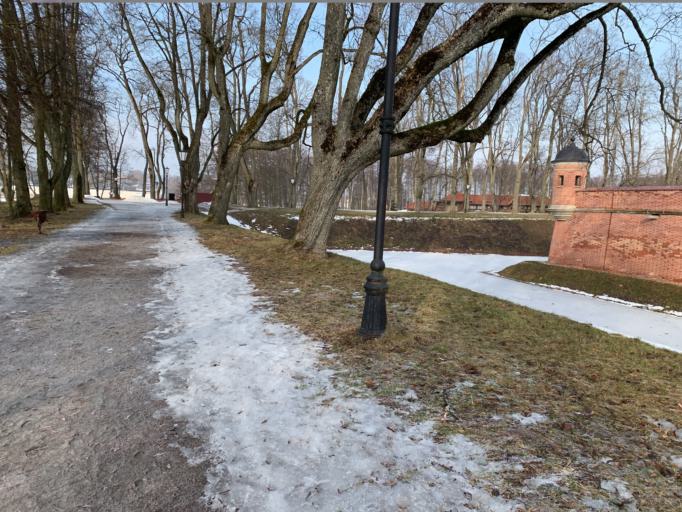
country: BY
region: Minsk
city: Nyasvizh
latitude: 53.2222
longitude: 26.6904
